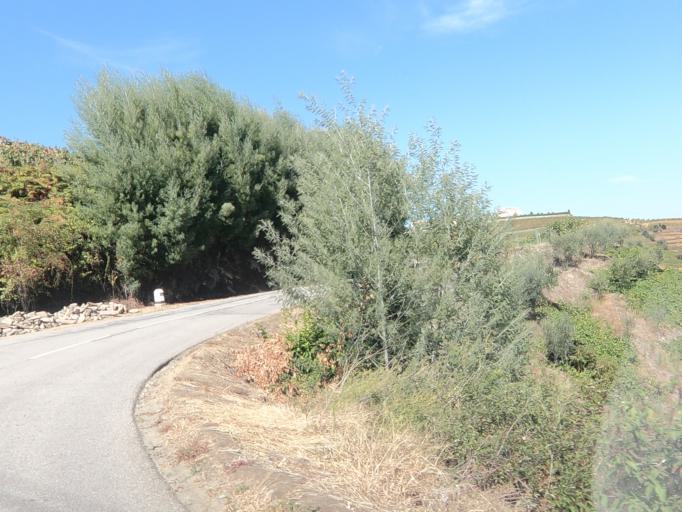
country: PT
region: Vila Real
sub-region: Santa Marta de Penaguiao
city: Santa Marta de Penaguiao
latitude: 41.2253
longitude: -7.7862
